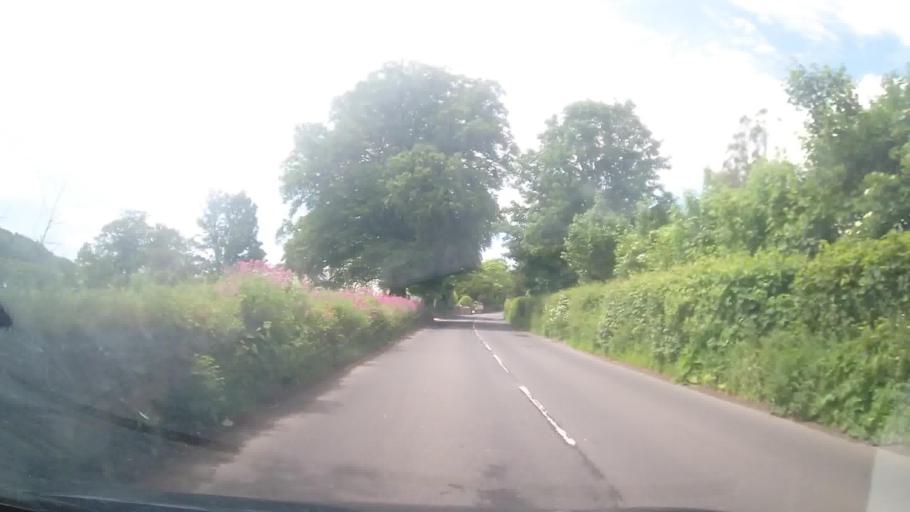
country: GB
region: England
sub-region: Devon
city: Modbury
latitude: 50.3613
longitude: -3.9106
